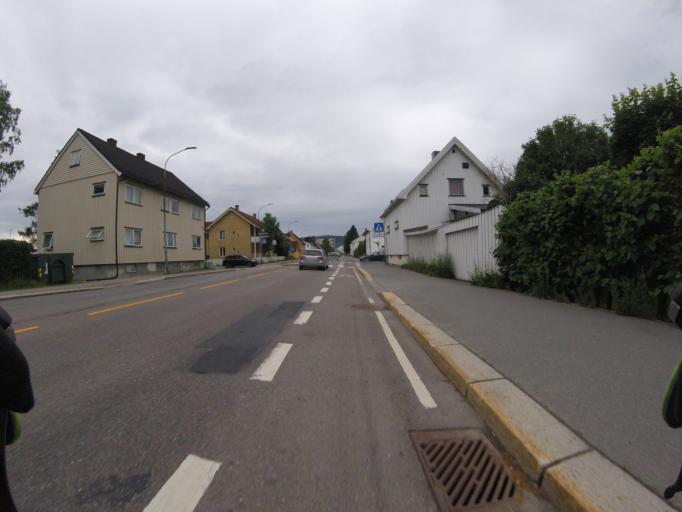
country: NO
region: Akershus
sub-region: Skedsmo
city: Lillestrom
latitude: 59.9635
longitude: 11.0511
